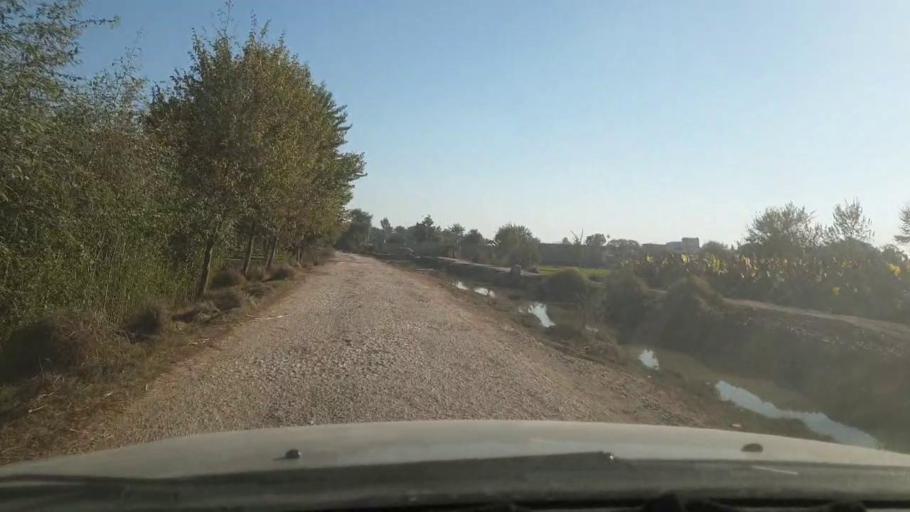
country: PK
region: Sindh
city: Adilpur
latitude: 27.9447
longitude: 69.2189
